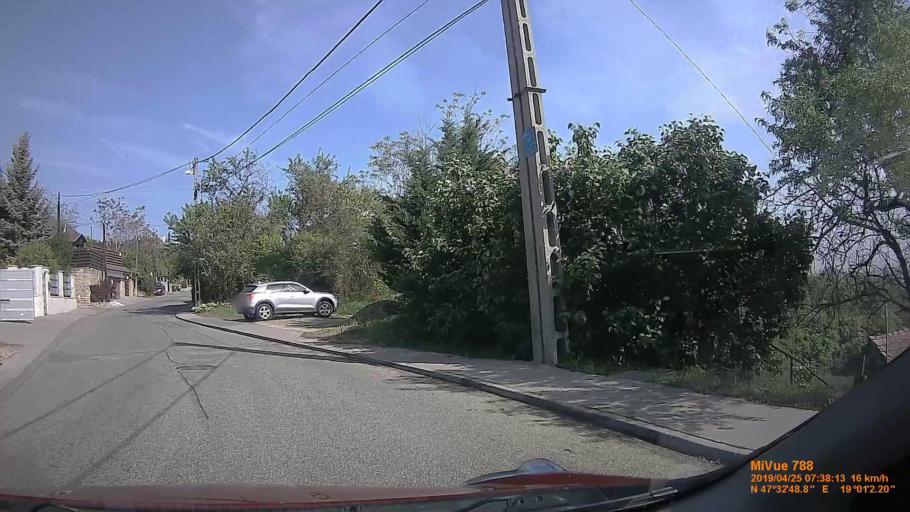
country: HU
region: Budapest
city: Budapest III. keruelet
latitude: 47.5470
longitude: 19.0172
